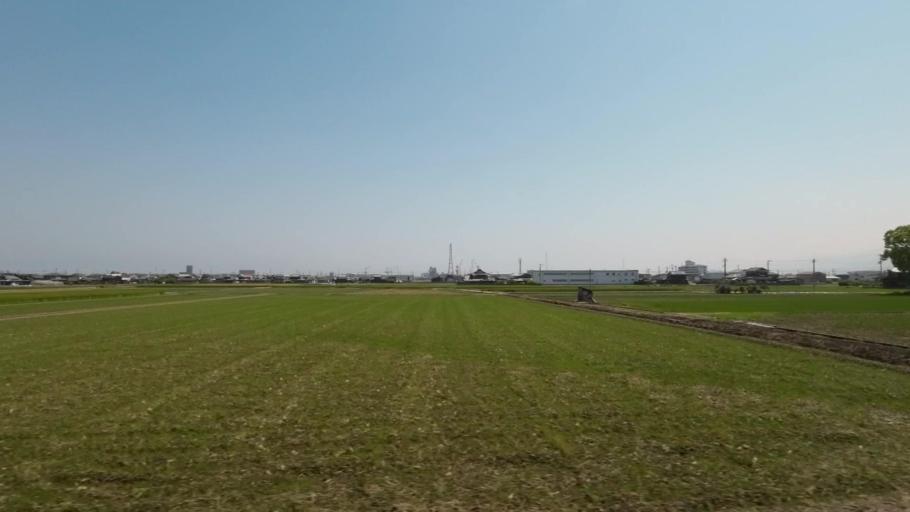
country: JP
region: Ehime
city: Saijo
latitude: 33.9209
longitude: 133.0934
